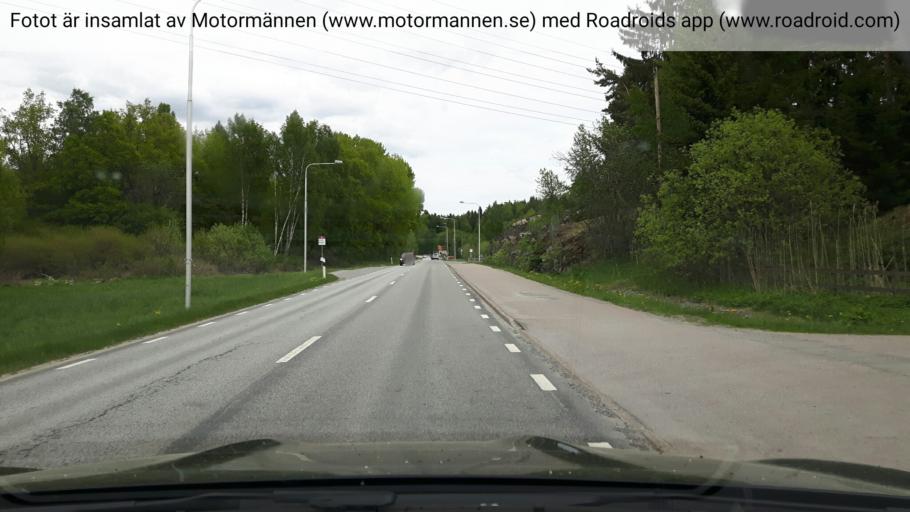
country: SE
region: Stockholm
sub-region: Osterakers Kommun
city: Akersberga
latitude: 59.5002
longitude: 18.3450
